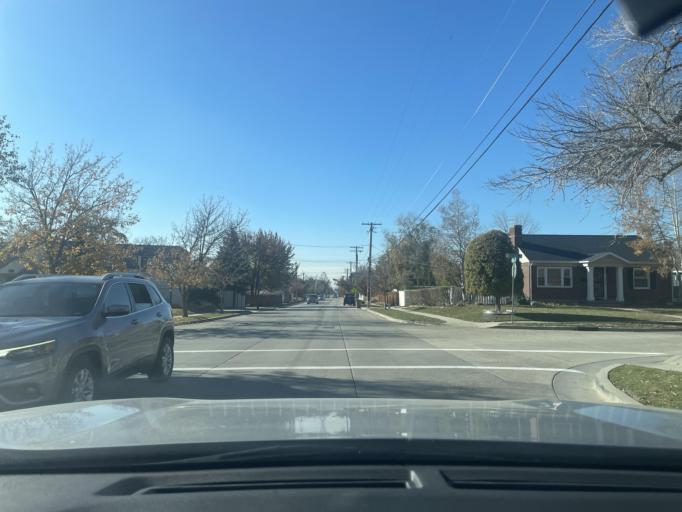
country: US
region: Utah
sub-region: Salt Lake County
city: Willard
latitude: 40.7417
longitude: -111.8339
